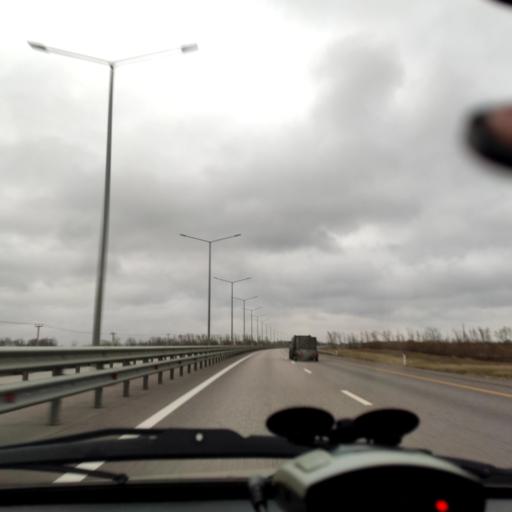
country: RU
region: Voronezj
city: Podkletnoye
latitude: 51.5826
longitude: 39.4584
